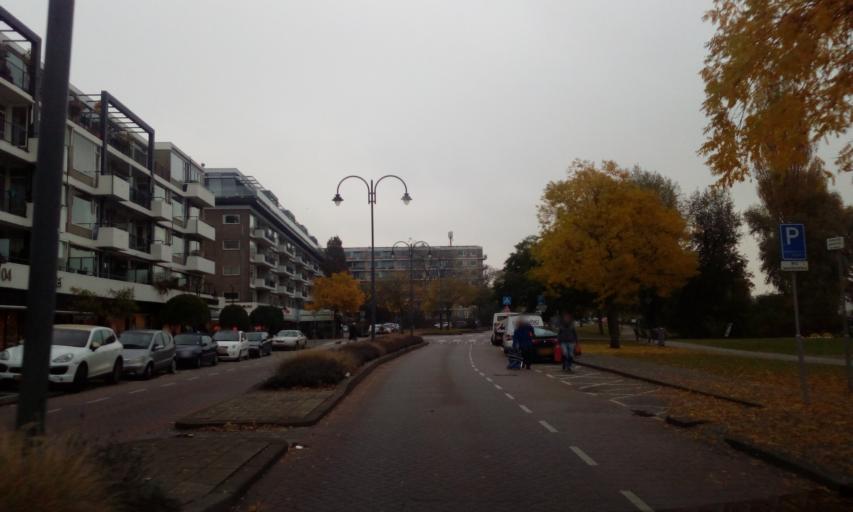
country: NL
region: South Holland
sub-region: Gemeente Lansingerland
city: Bergschenhoek
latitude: 51.9561
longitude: 4.4955
